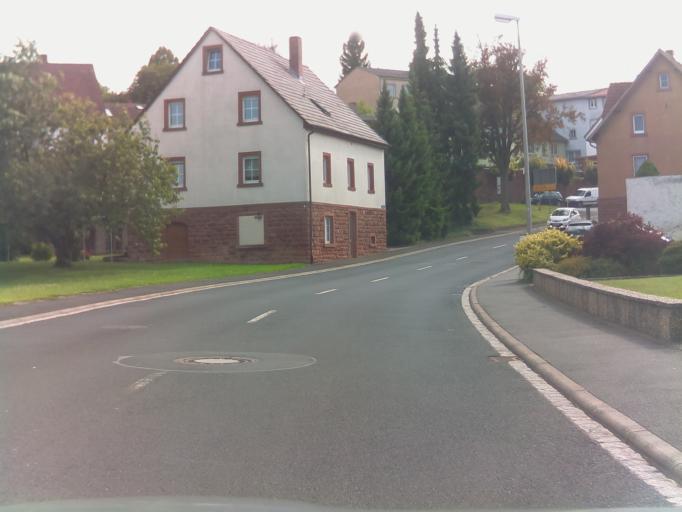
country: DE
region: Bavaria
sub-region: Regierungsbezirk Unterfranken
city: Neubrunn
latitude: 49.7327
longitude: 9.6767
